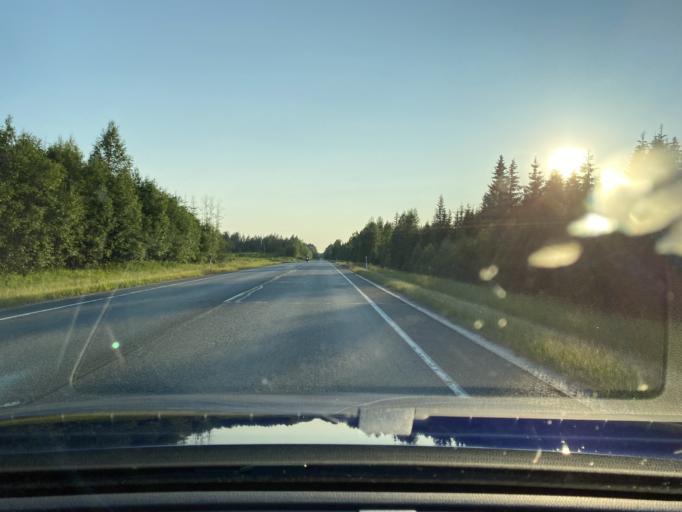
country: FI
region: Haeme
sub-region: Forssa
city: Tammela
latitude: 60.8258
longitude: 23.9565
